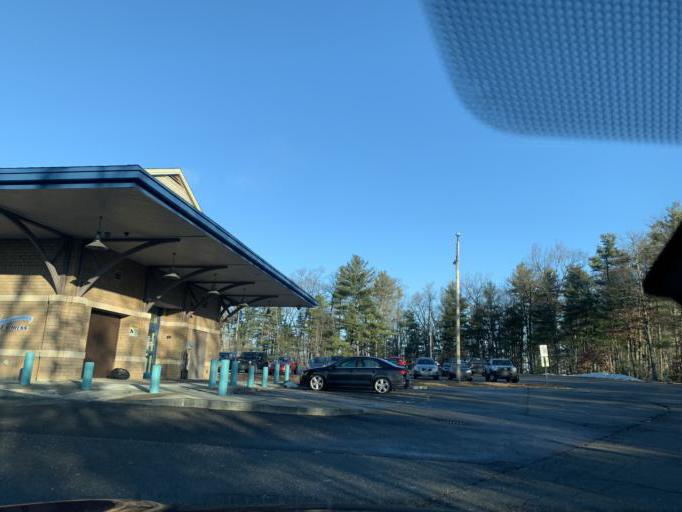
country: US
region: New Hampshire
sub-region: Rockingham County
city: Derry
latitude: 42.8714
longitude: -71.3442
